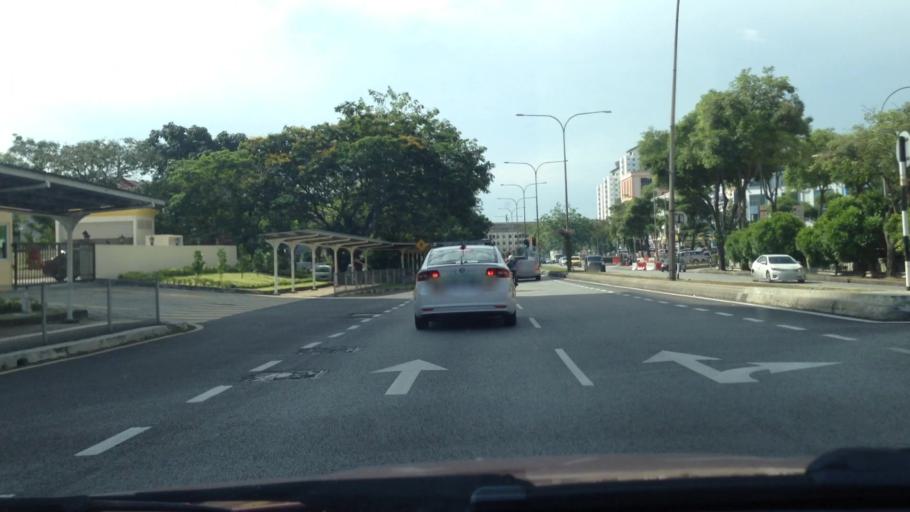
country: MY
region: Selangor
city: Subang Jaya
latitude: 3.0490
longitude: 101.5865
